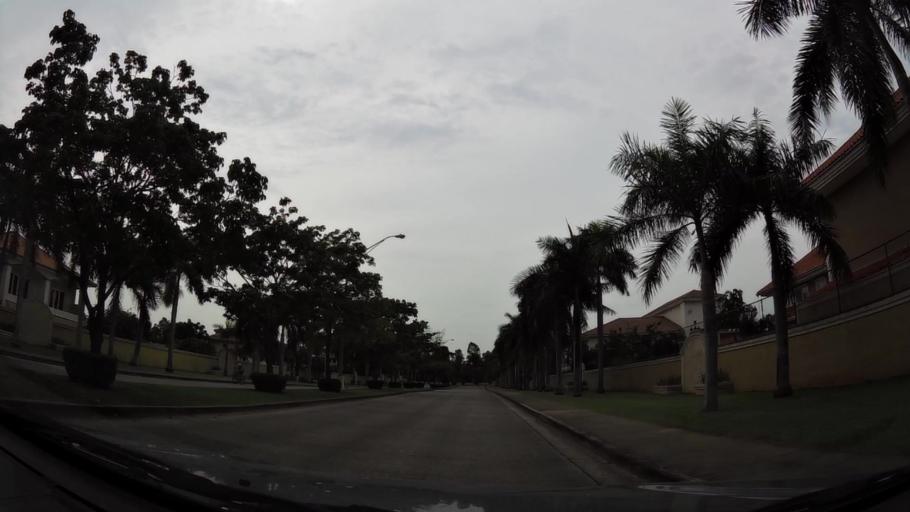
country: PA
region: Panama
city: San Miguelito
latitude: 9.0127
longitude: -79.4588
